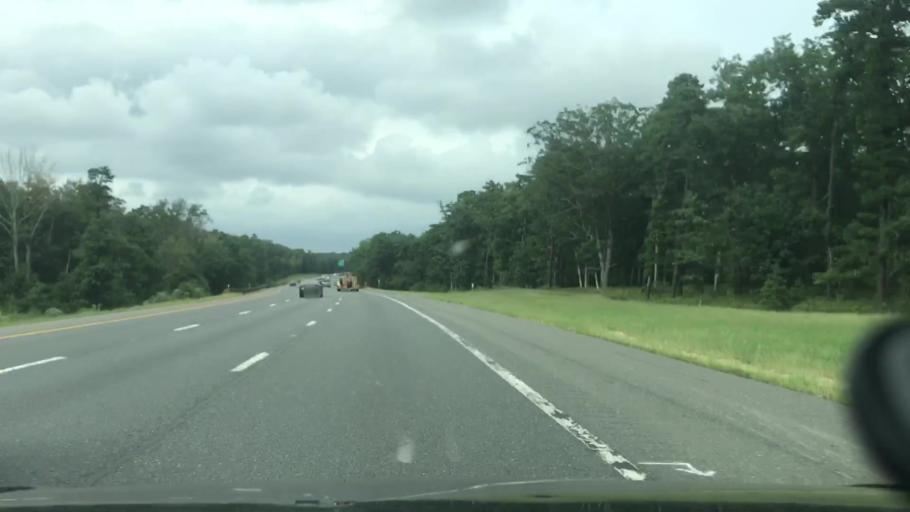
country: US
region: New Jersey
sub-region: Ocean County
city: Barnegat
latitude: 39.7787
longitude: -74.2428
